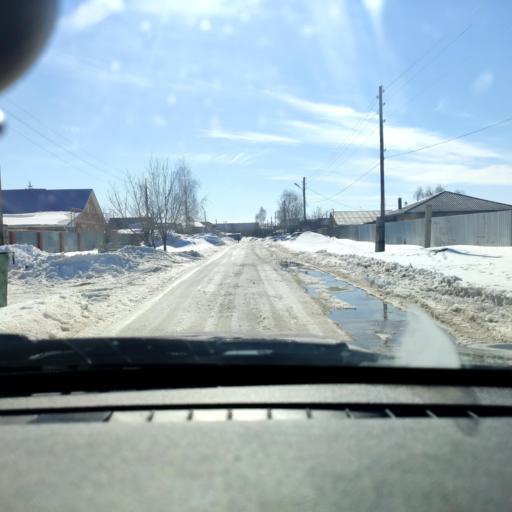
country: RU
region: Samara
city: Tol'yatti
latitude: 53.5689
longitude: 49.3228
